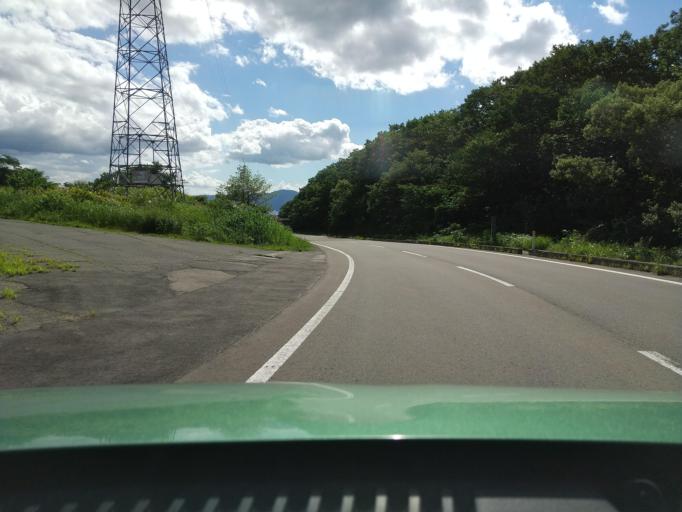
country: JP
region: Iwate
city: Shizukuishi
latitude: 39.7657
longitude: 140.7491
